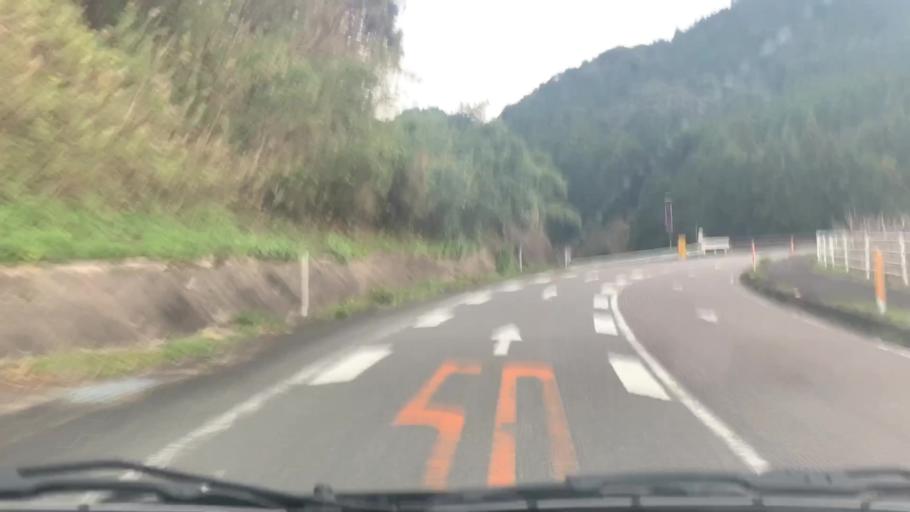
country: JP
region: Saga Prefecture
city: Kashima
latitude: 33.0503
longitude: 130.0739
